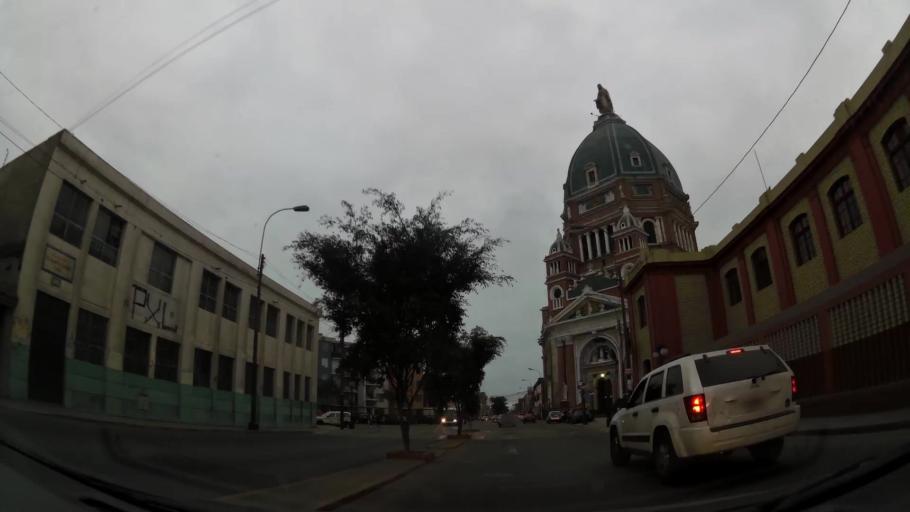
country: PE
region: Lima
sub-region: Lima
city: San Isidro
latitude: -12.0863
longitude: -77.0685
